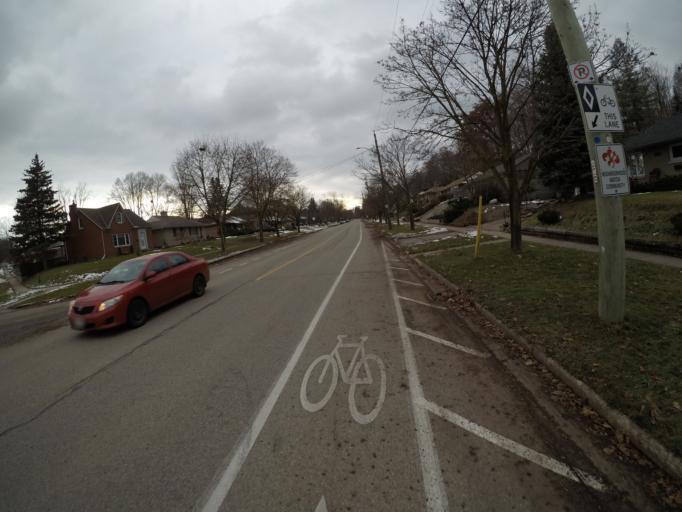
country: CA
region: Ontario
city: Waterloo
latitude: 43.4709
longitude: -80.4898
